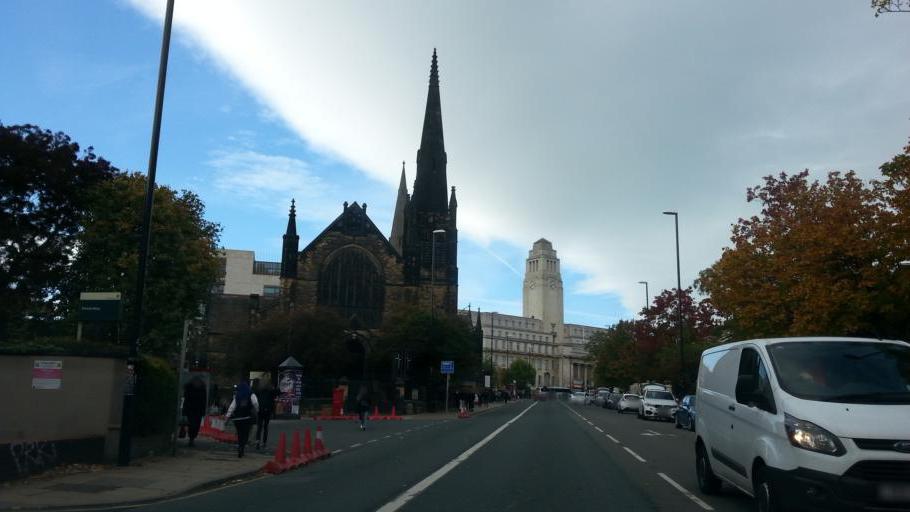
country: GB
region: England
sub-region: City and Borough of Leeds
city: Leeds
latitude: 53.8062
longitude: -1.5500
